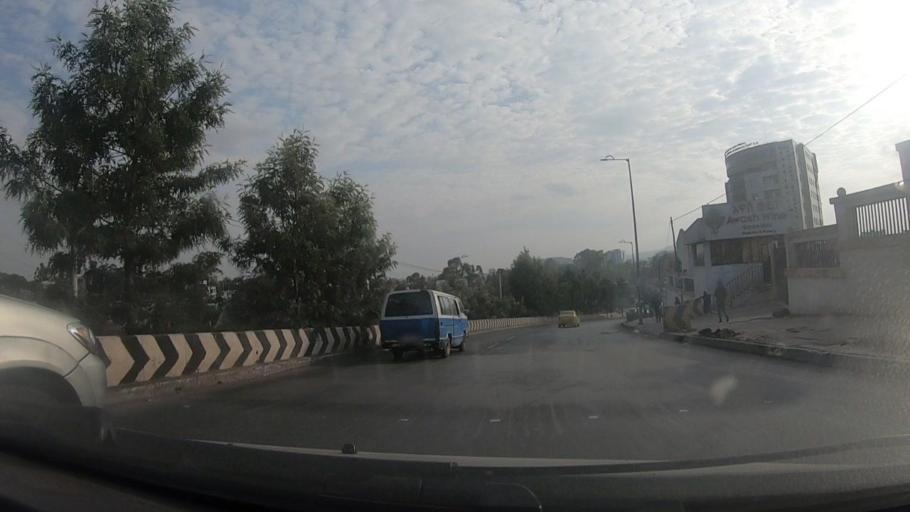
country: ET
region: Adis Abeba
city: Addis Ababa
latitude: 8.9766
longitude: 38.7341
